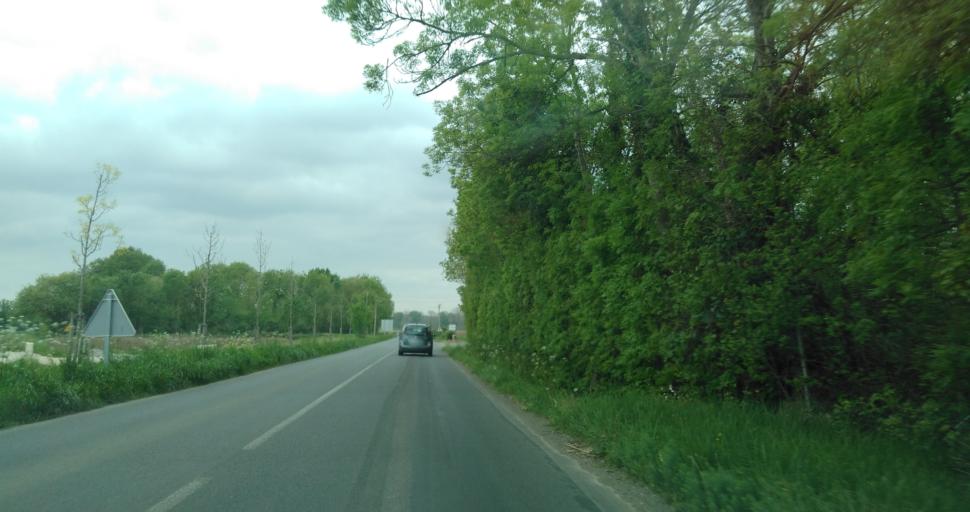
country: FR
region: Poitou-Charentes
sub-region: Departement des Deux-Sevres
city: Magne
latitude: 46.3174
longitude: -0.5585
